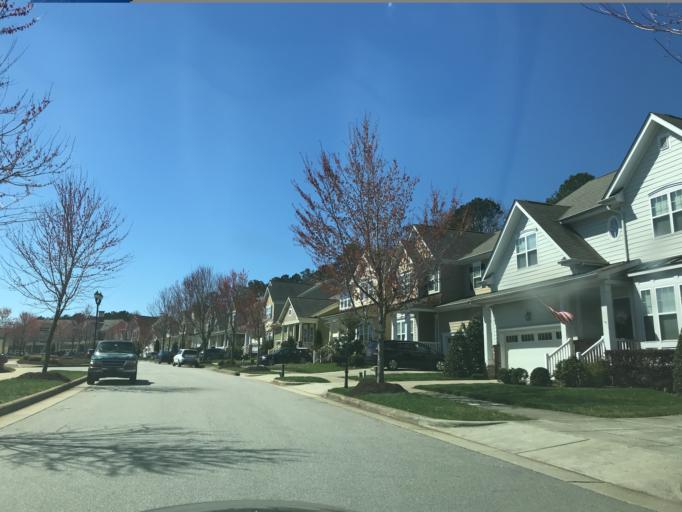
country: US
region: North Carolina
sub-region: Wake County
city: Raleigh
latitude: 35.7382
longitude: -78.6612
